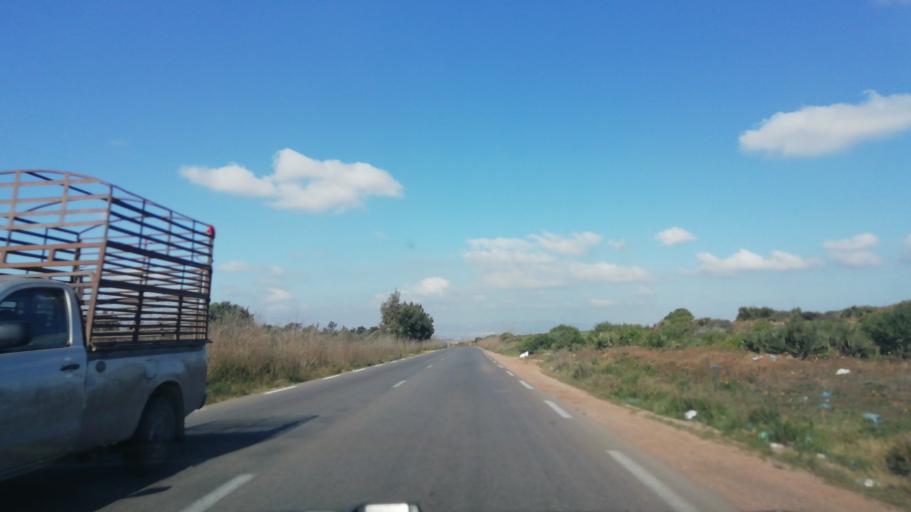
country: DZ
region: Oran
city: Ain el Bya
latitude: 35.7192
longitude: -0.2376
